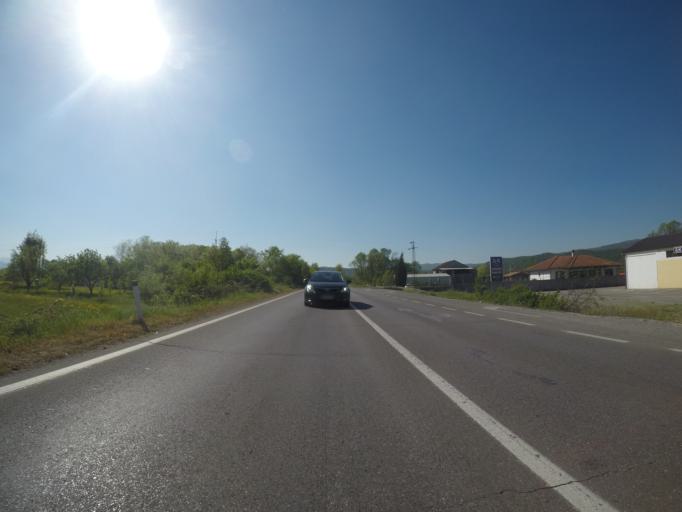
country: ME
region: Danilovgrad
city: Danilovgrad
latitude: 42.5275
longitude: 19.1177
